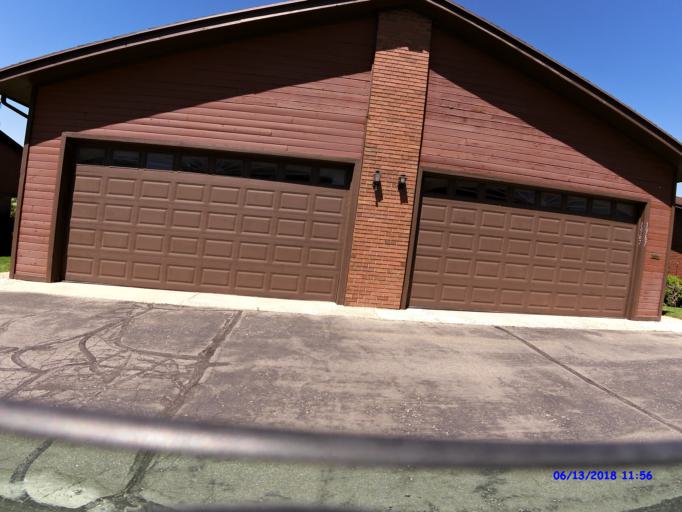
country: US
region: Utah
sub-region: Weber County
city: Ogden
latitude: 41.2312
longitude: -111.9450
